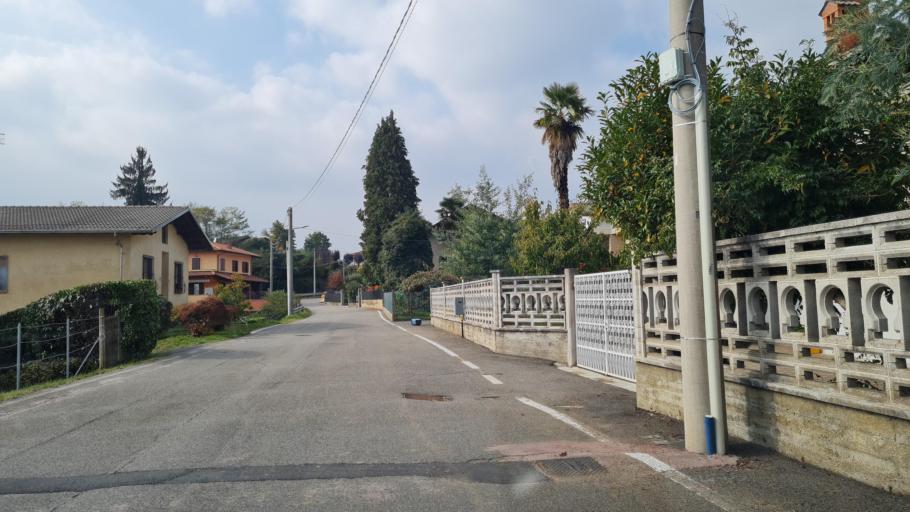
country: IT
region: Piedmont
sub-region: Provincia di Biella
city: Lessona
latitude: 45.5973
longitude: 8.1946
